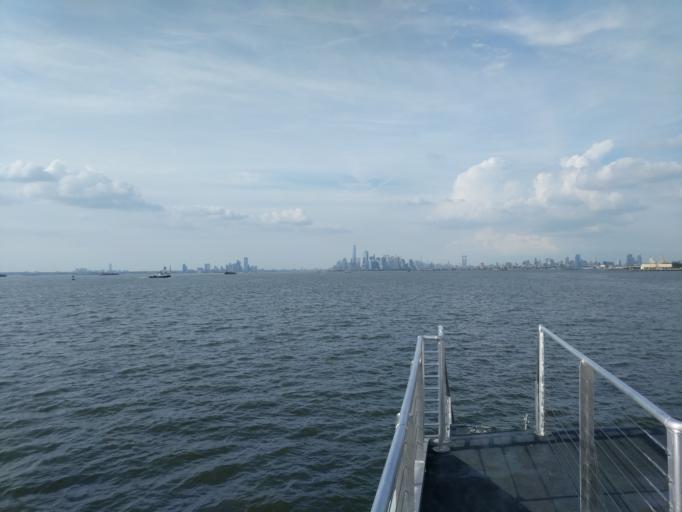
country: US
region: New York
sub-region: Kings County
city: Bensonhurst
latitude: 40.6405
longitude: -74.0397
